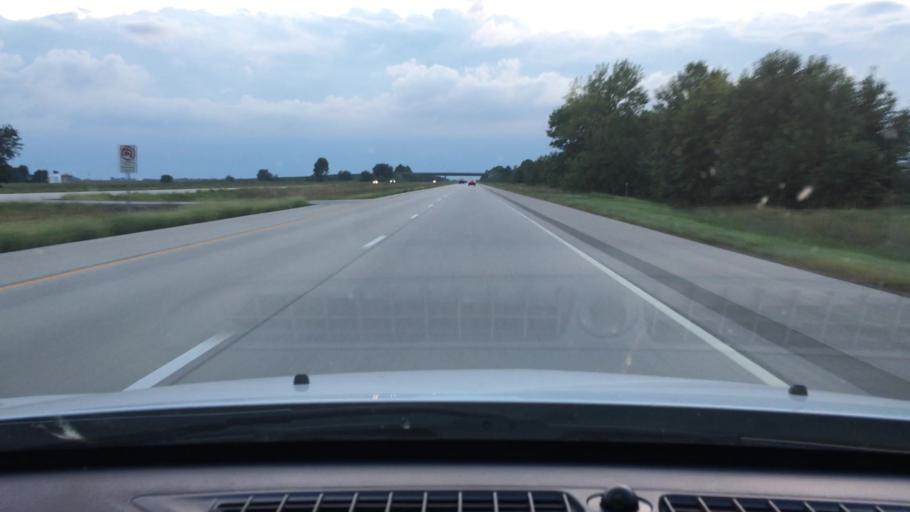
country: US
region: Illinois
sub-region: Sangamon County
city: New Berlin
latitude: 39.7413
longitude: -89.8364
